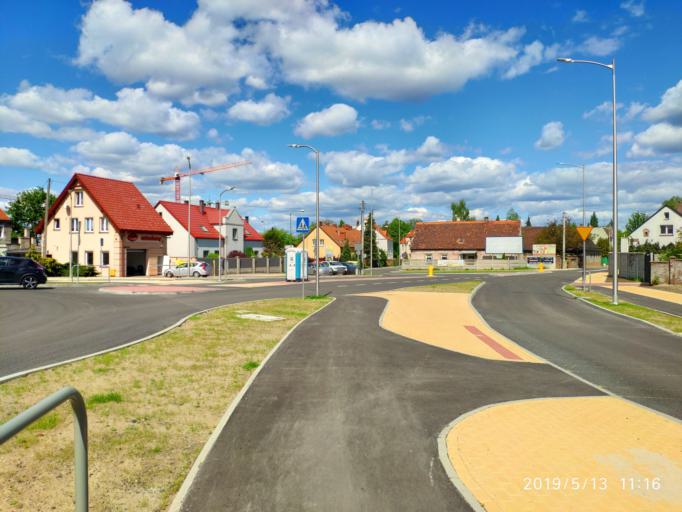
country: PL
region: Lubusz
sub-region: Zielona Gora
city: Zielona Gora
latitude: 51.9455
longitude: 15.5026
